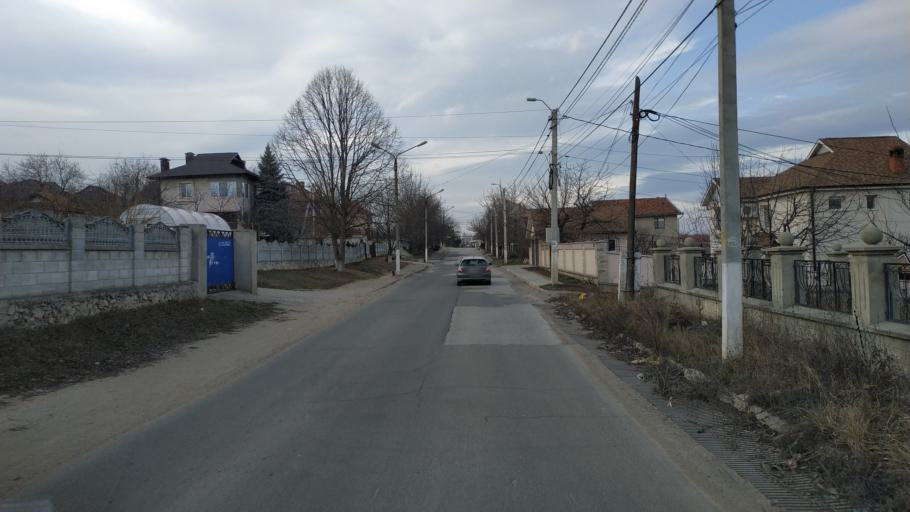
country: MD
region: Laloveni
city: Ialoveni
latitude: 46.9594
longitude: 28.7572
